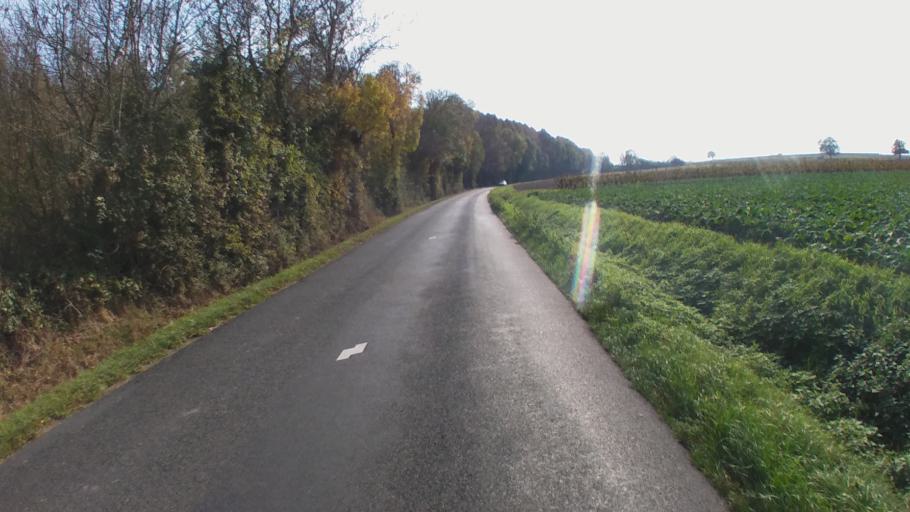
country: FR
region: Pays de la Loire
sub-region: Departement de Maine-et-Loire
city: Distre
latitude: 47.2190
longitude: -0.0913
